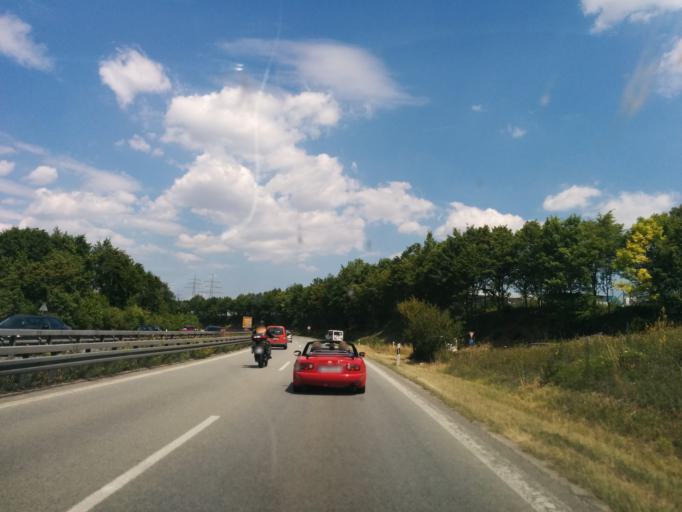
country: DE
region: Bavaria
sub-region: Swabia
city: Augsburg
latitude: 48.3382
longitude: 10.8897
